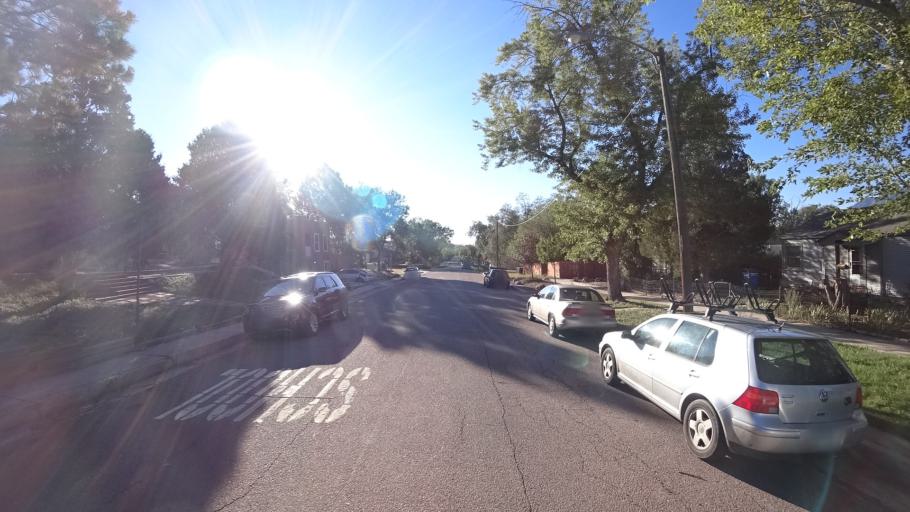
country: US
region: Colorado
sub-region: El Paso County
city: Colorado Springs
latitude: 38.8442
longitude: -104.8509
